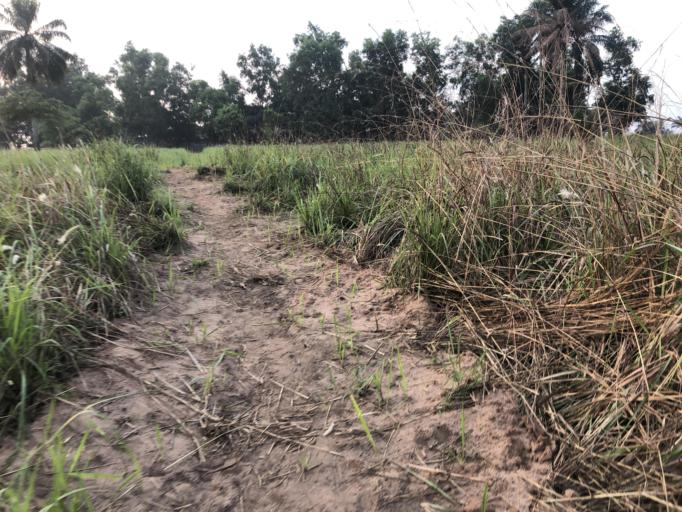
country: CD
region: Bandundu
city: Kikwit
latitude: -5.0732
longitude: 18.8484
